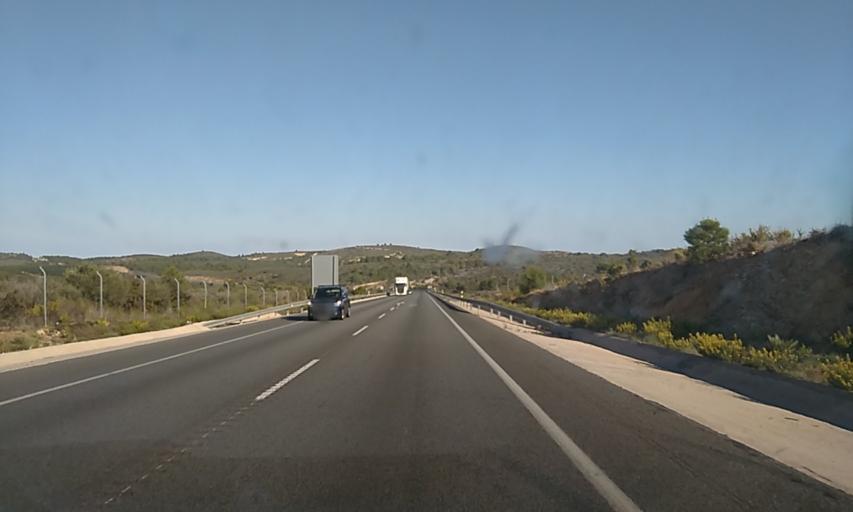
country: ES
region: Valencia
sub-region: Provincia de Castello
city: Torreblanca
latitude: 40.2107
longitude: 0.1316
